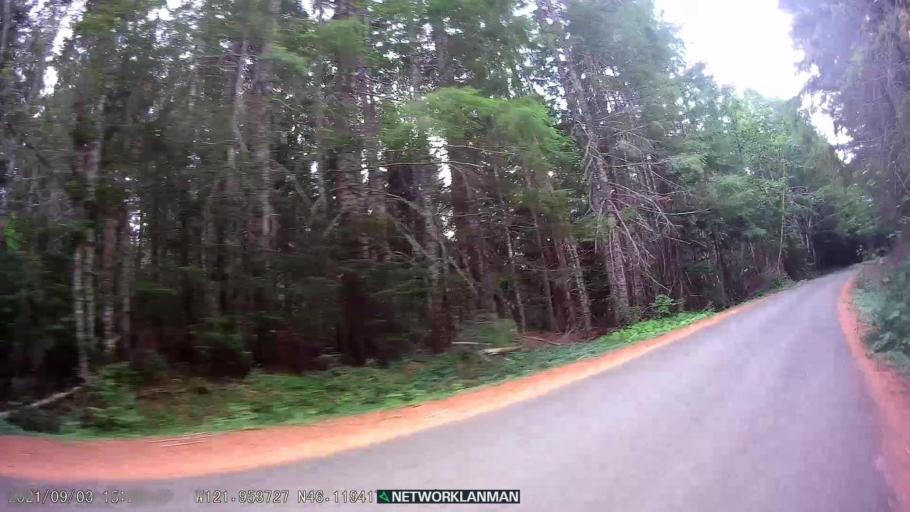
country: US
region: Washington
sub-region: Skamania County
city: Carson
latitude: 46.1193
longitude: -121.9537
